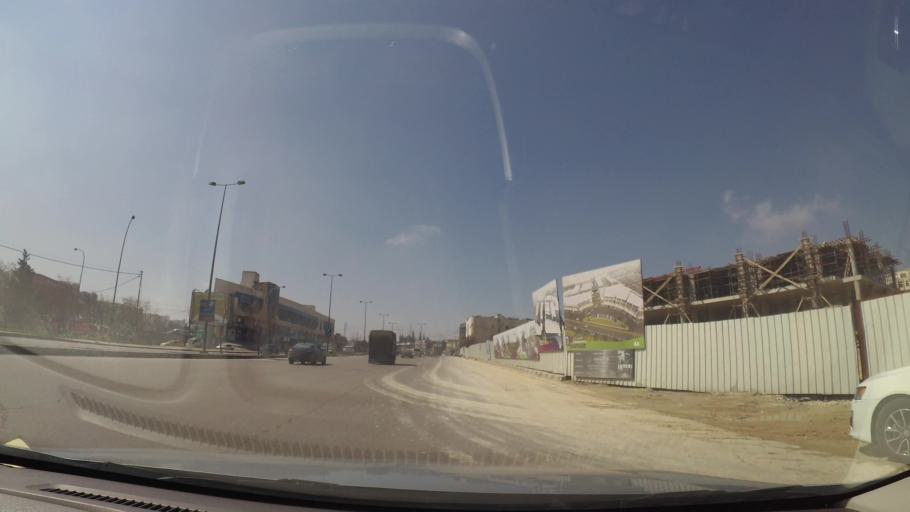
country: JO
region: Amman
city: Al Bunayyat ash Shamaliyah
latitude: 31.9175
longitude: 35.9064
